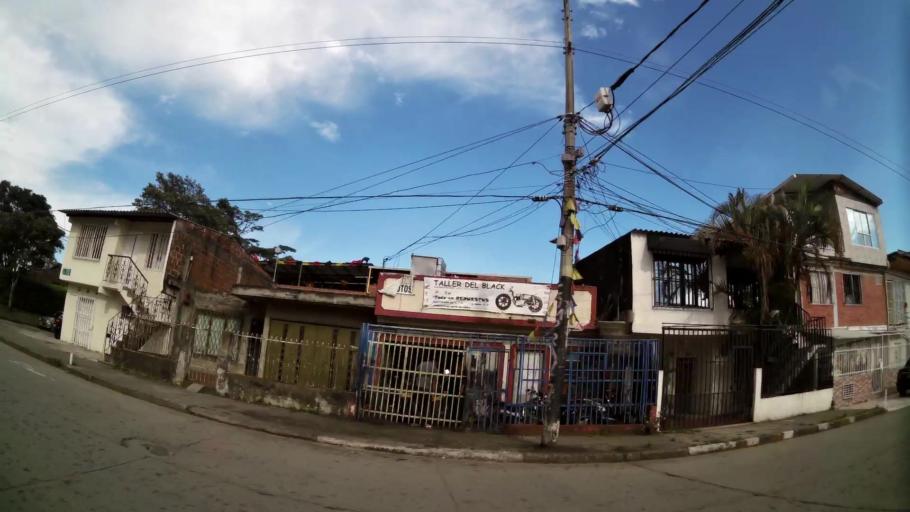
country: CO
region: Valle del Cauca
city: Cali
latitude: 3.4217
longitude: -76.5215
